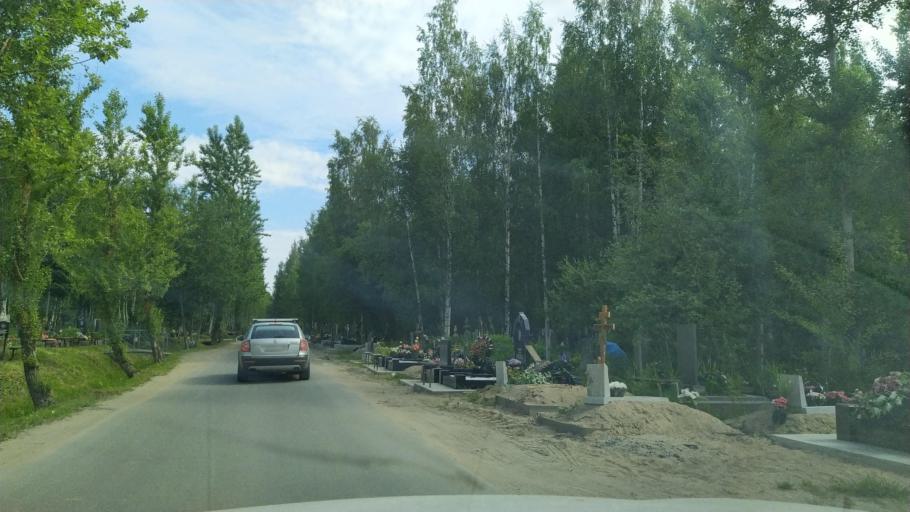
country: RU
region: St.-Petersburg
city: Dachnoye
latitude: 59.7678
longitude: 30.2632
